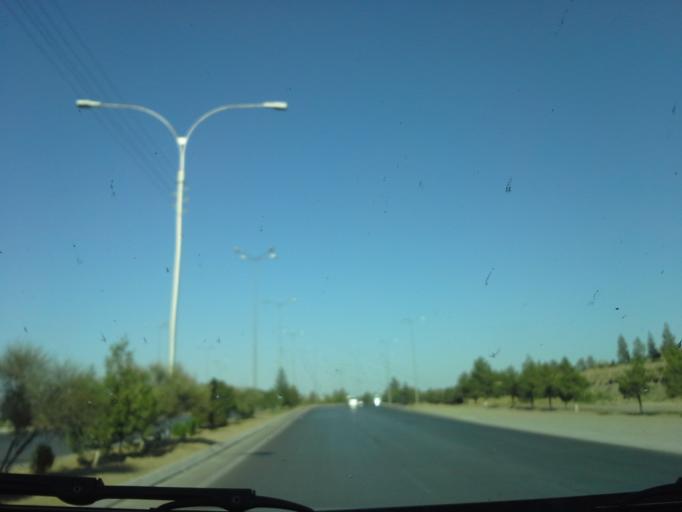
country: TM
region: Ahal
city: Ashgabat
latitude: 37.9705
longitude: 58.2739
